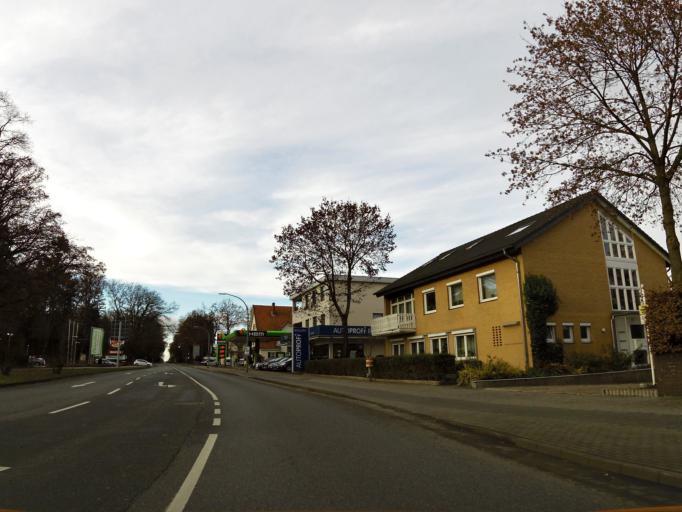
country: DE
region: Lower Saxony
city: Munster
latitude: 52.9906
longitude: 10.0808
